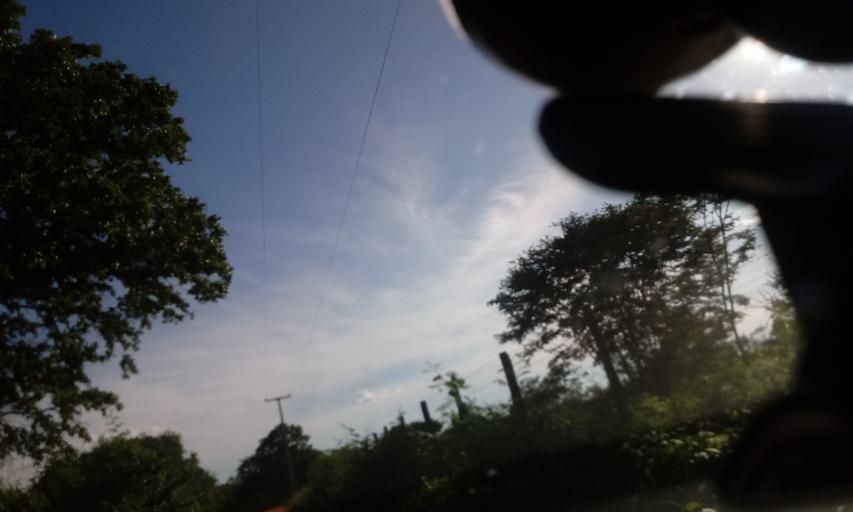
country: BR
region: Bahia
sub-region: Riacho De Santana
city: Riacho de Santana
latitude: -13.8592
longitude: -42.7790
